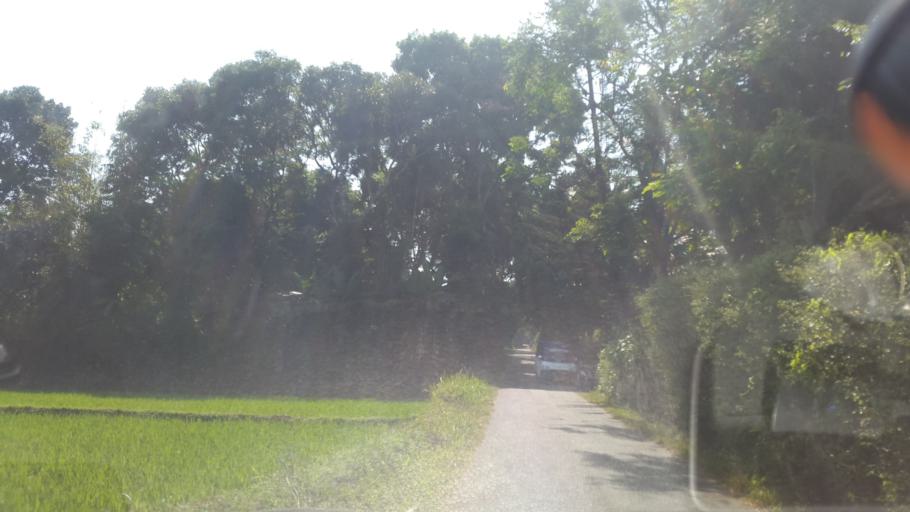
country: ID
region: West Java
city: Cicurug
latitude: -6.8385
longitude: 106.8299
